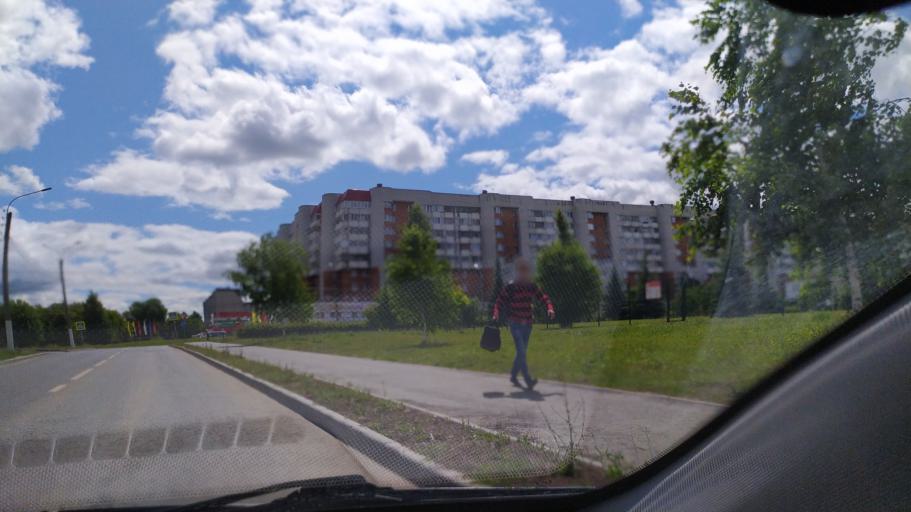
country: RU
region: Chuvashia
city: Novyye Lapsary
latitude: 56.1226
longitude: 47.1889
